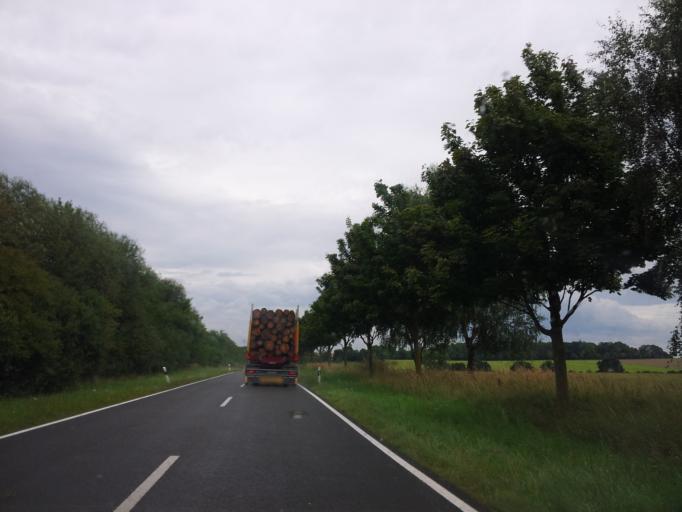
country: DE
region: Brandenburg
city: Wiesenburg
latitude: 52.1584
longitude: 12.5159
